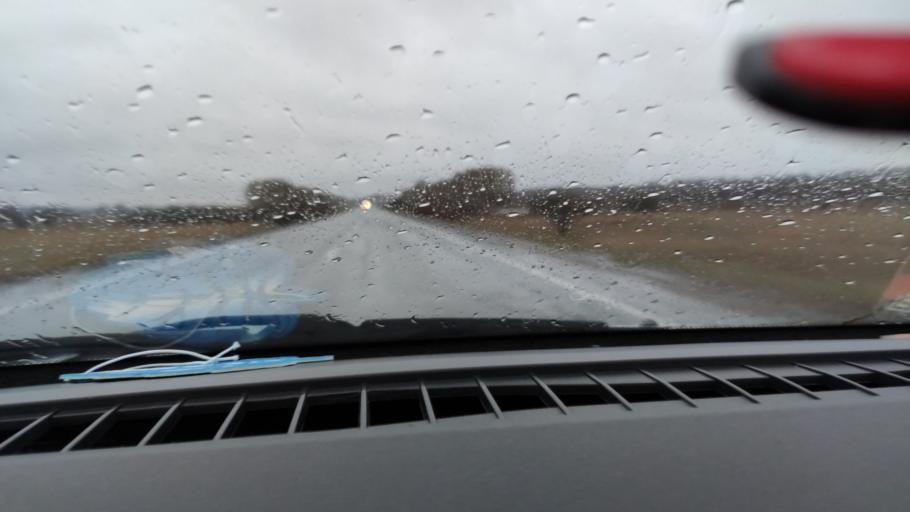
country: RU
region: Tatarstan
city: Mendeleyevsk
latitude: 55.9660
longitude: 52.3162
